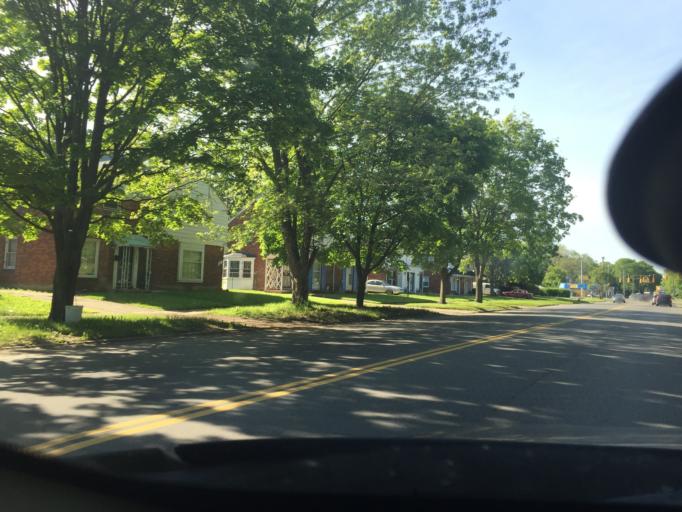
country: US
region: Michigan
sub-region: Oakland County
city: Southfield
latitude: 42.4134
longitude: -83.2380
